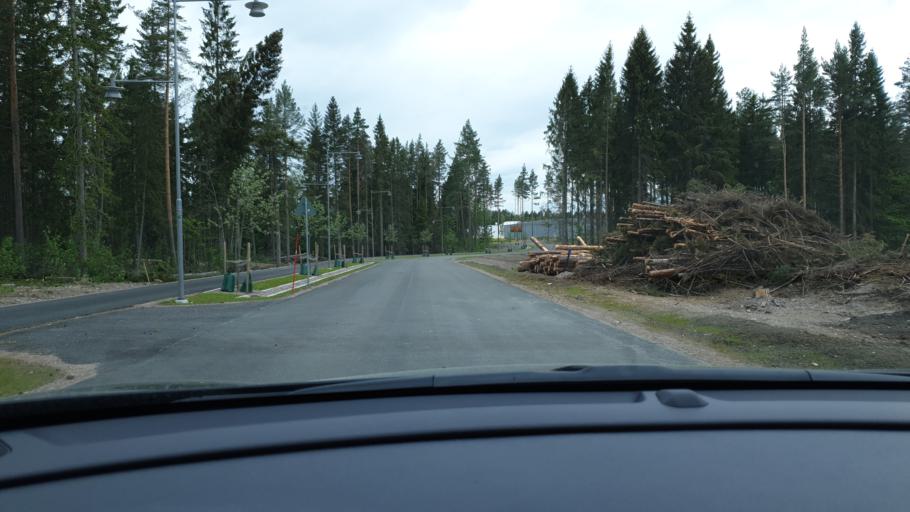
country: SE
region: Gaevleborg
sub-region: Gavle Kommun
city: Gavle
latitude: 60.6421
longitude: 17.1503
